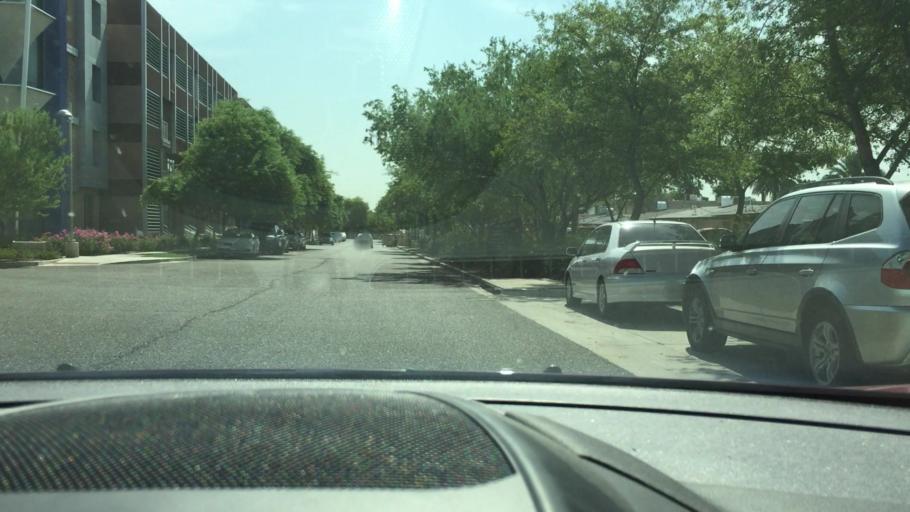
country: US
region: Arizona
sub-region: Maricopa County
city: Tempe
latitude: 33.4621
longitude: -111.9243
